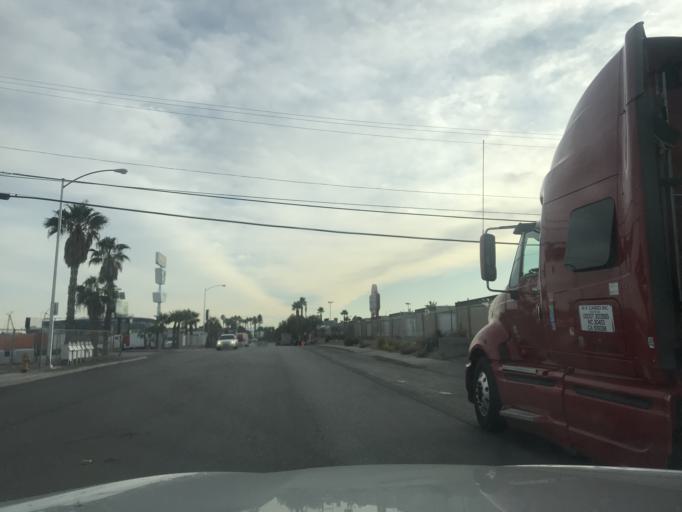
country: US
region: Nevada
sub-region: Clark County
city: Paradise
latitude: 36.1030
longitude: -115.1877
